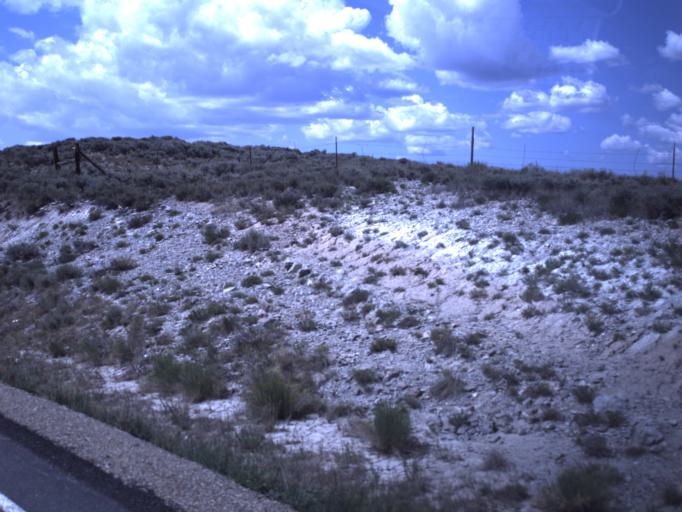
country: US
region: Utah
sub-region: Carbon County
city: Helper
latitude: 39.8038
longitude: -110.7814
